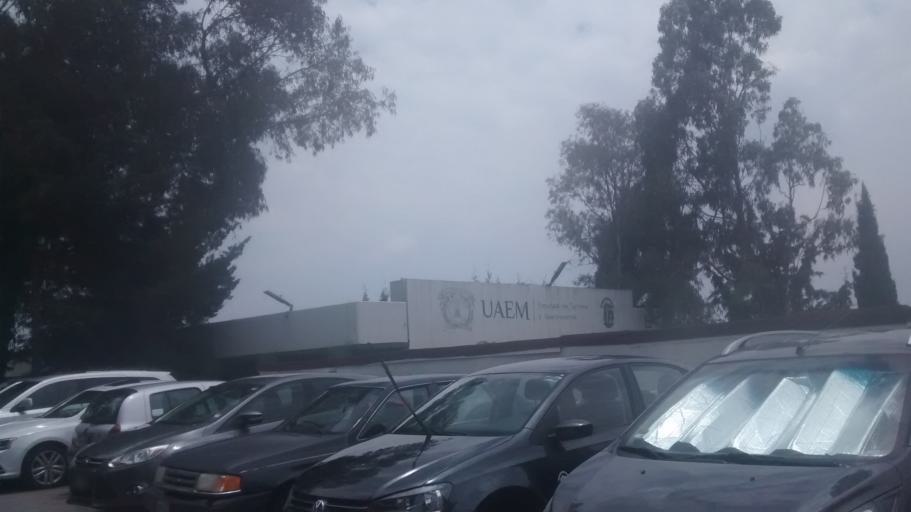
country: MX
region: Mexico
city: San Buenaventura
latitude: 19.2828
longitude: -99.6783
